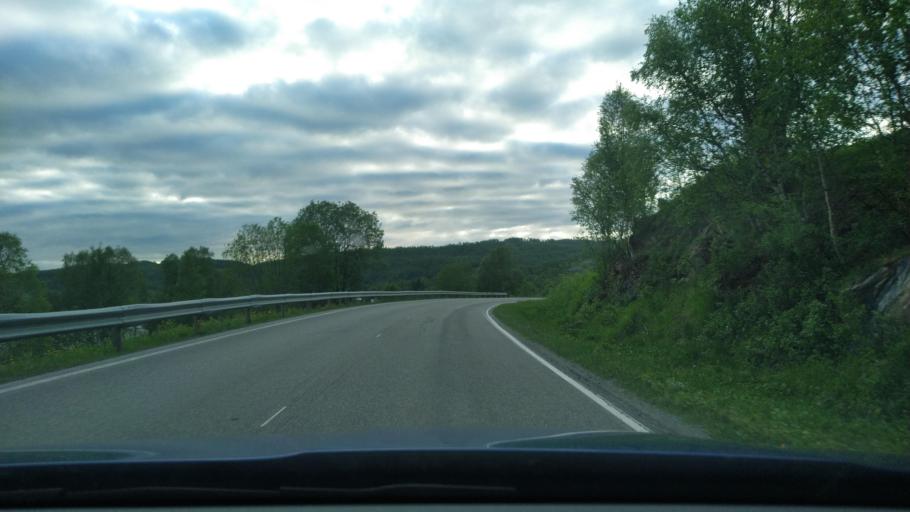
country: NO
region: Troms
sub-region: Sorreisa
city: Sorreisa
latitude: 69.0918
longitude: 18.3424
